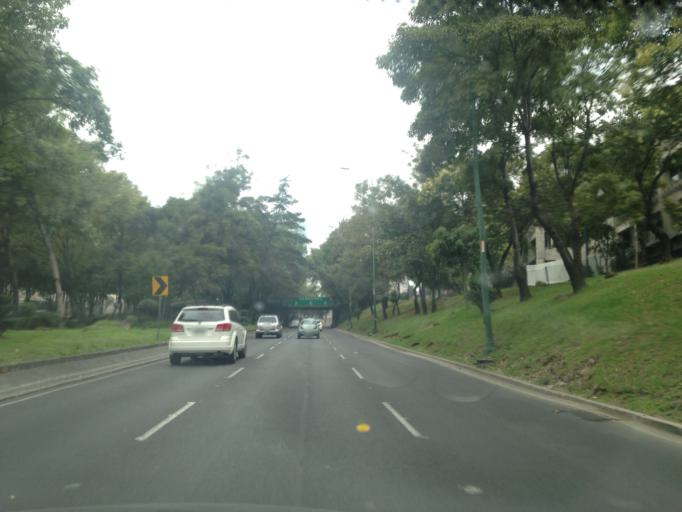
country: MX
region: Mexico City
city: Benito Juarez
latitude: 19.3981
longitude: -99.1762
